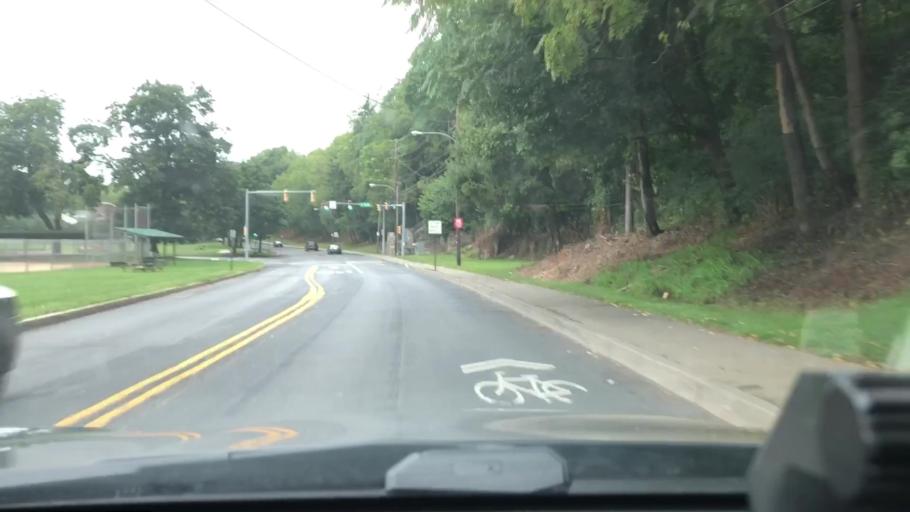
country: US
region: Pennsylvania
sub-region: Lehigh County
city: Allentown
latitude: 40.5980
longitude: -75.4749
